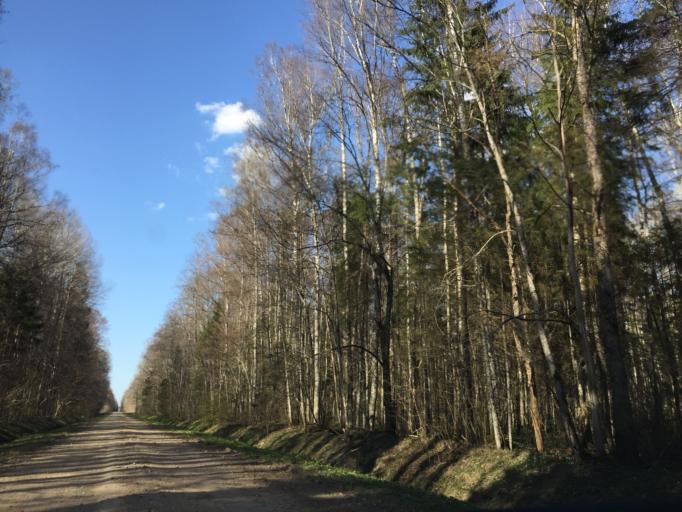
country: LV
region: Kegums
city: Kegums
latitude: 56.8571
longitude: 24.8021
